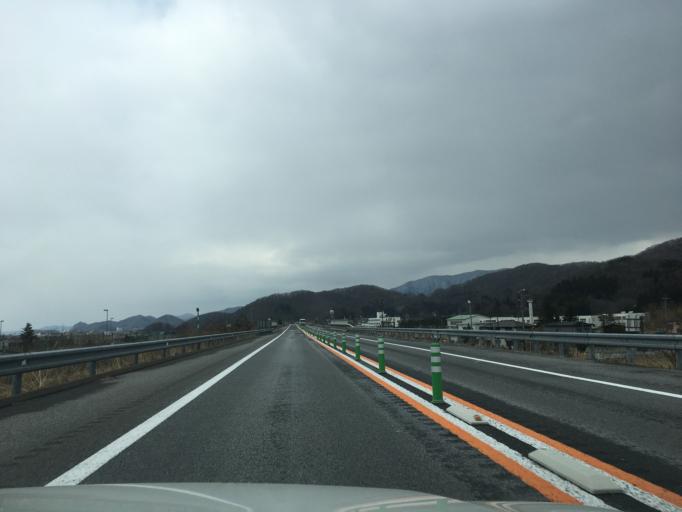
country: JP
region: Aomori
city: Aomori Shi
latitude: 40.8071
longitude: 140.7983
